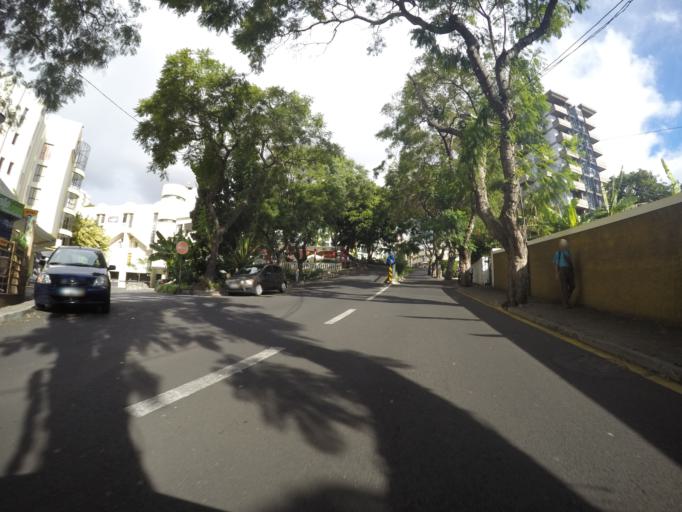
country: PT
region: Madeira
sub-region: Funchal
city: Funchal
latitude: 32.6372
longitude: -16.9311
